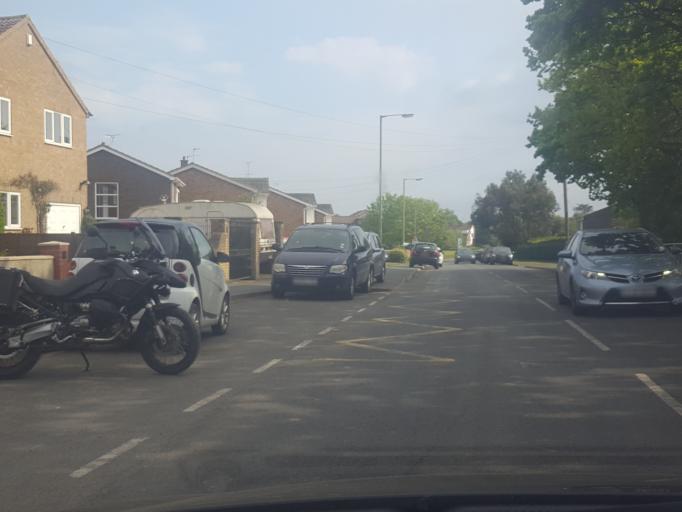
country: GB
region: England
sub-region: Essex
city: Frinton-on-Sea
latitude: 51.8464
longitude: 1.2477
